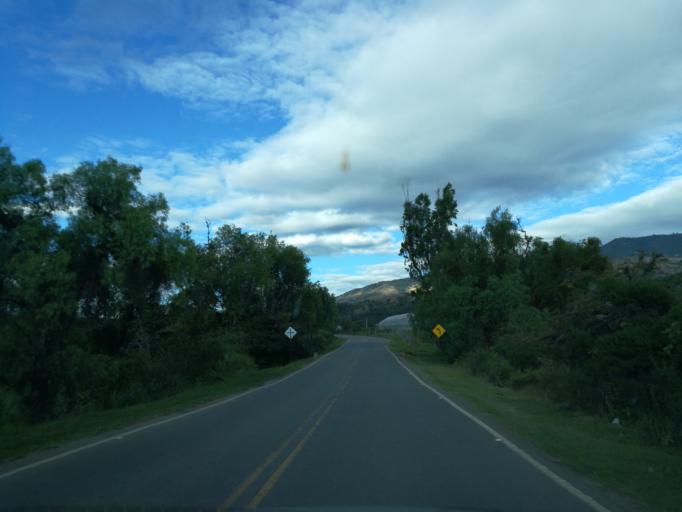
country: CO
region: Boyaca
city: Sutamarchan
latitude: 5.6127
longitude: -73.6259
